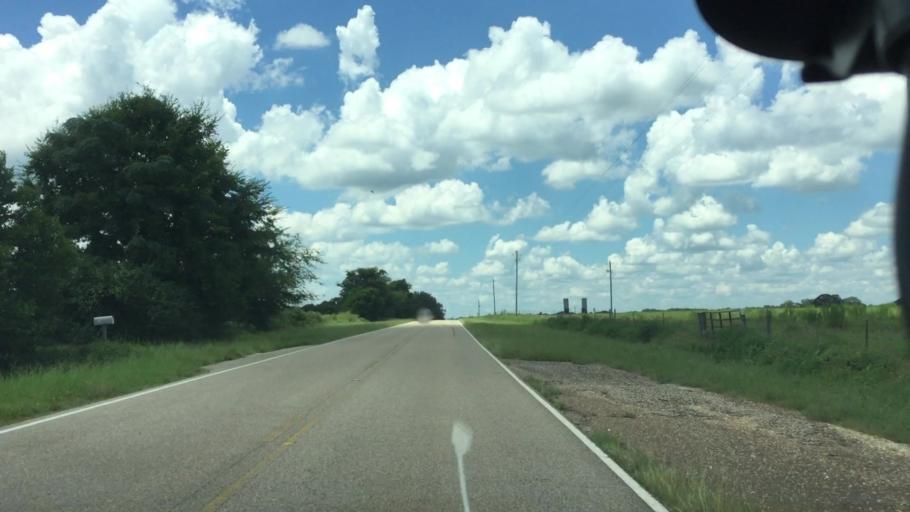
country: US
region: Alabama
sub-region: Coffee County
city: New Brockton
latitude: 31.4147
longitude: -85.8711
